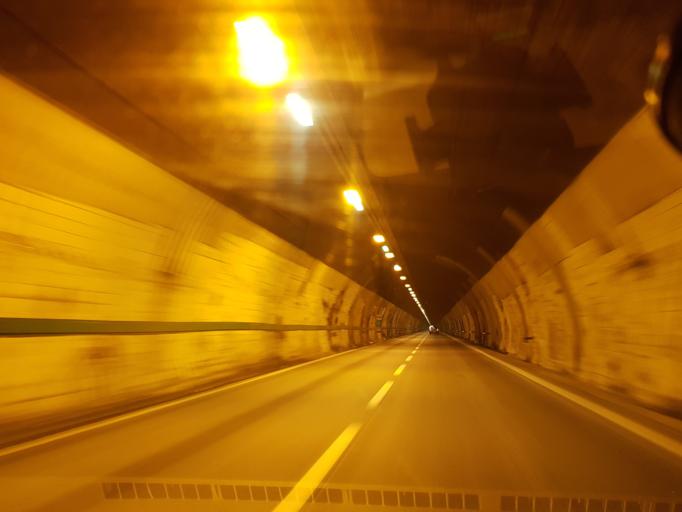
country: IT
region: Liguria
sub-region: Provincia di Genova
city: Isola del Cantone
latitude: 44.6651
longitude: 8.9270
